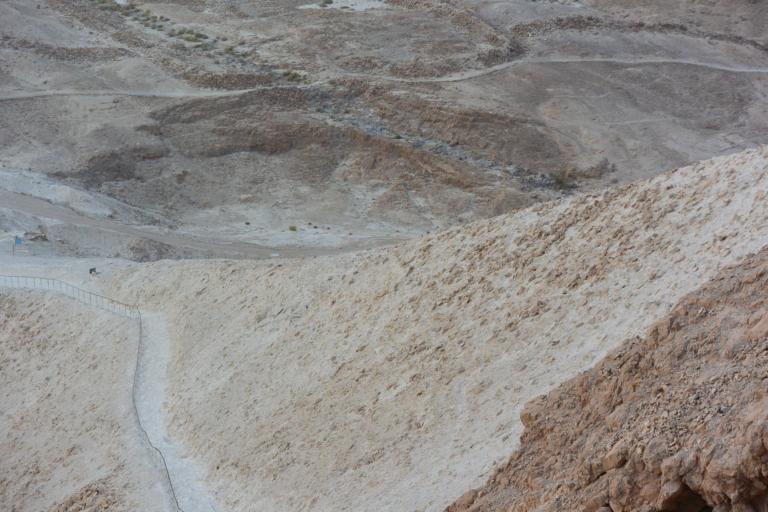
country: IL
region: Southern District
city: `En Boqeq
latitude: 31.3162
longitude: 35.3526
